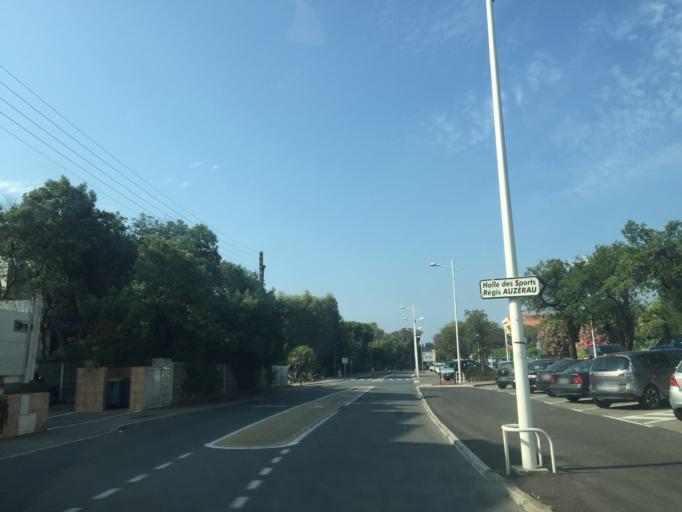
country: FR
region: Provence-Alpes-Cote d'Azur
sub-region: Departement du Var
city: Frejus
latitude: 43.3826
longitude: 6.7223
